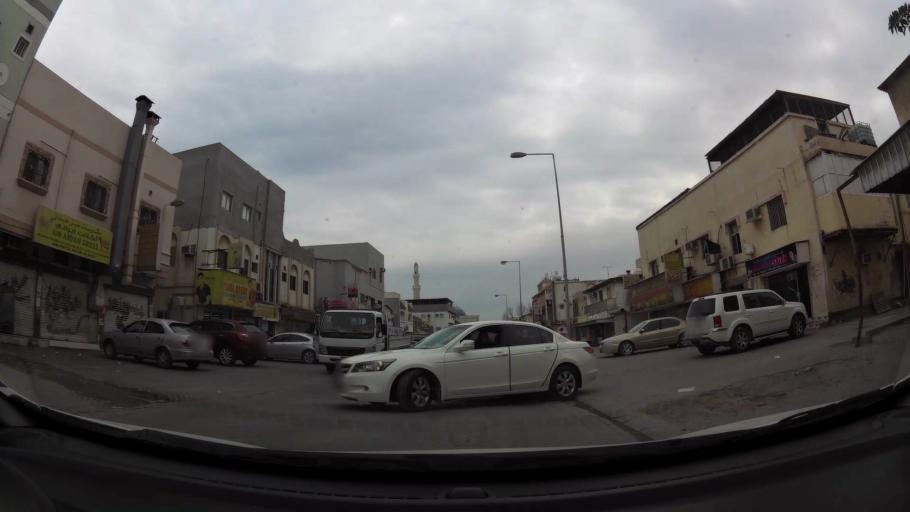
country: BH
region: Northern
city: Sitrah
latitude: 26.1642
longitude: 50.6143
